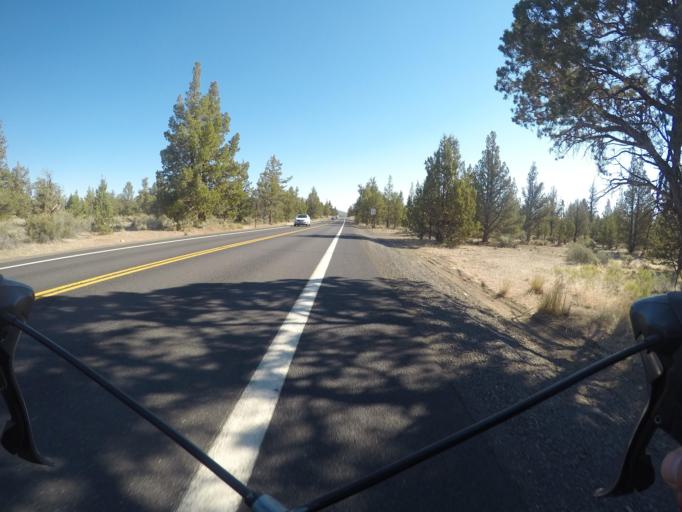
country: US
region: Oregon
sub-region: Deschutes County
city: Redmond
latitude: 44.2190
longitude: -121.3130
